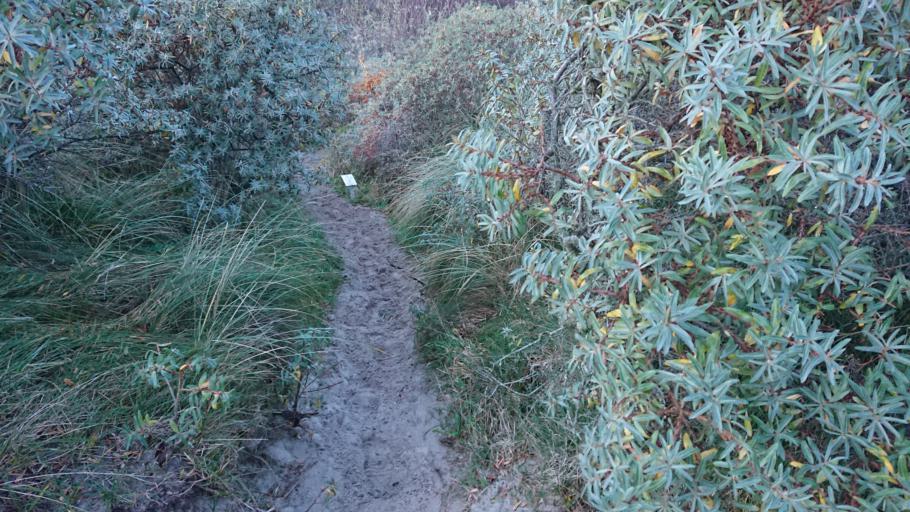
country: DK
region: North Denmark
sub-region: Frederikshavn Kommune
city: Skagen
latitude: 57.7441
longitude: 10.6365
